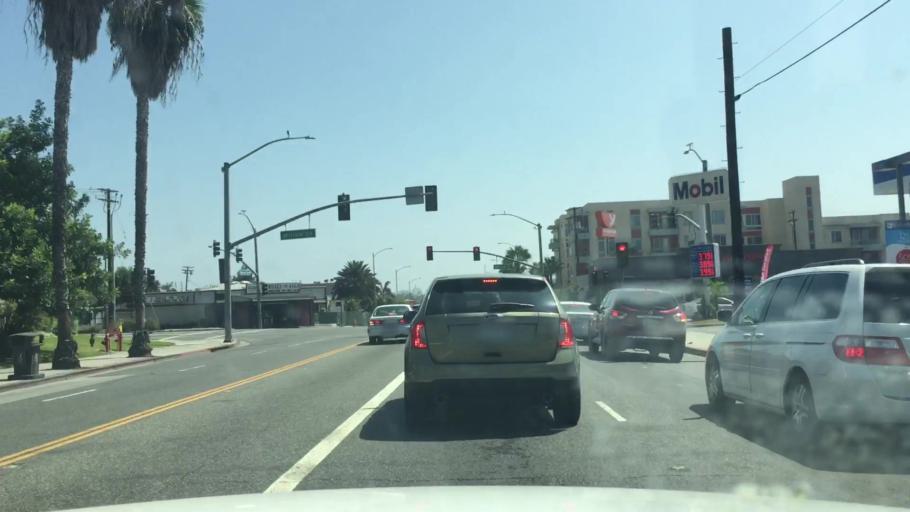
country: US
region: California
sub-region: Los Angeles County
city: Signal Hill
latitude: 33.8050
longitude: -118.1851
